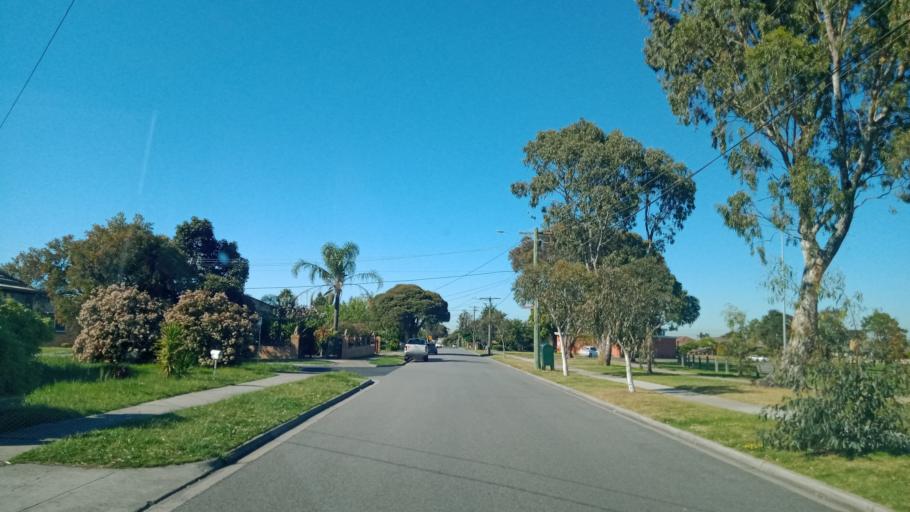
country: AU
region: Victoria
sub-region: Greater Dandenong
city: Springvale
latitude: -37.9360
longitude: 145.1690
